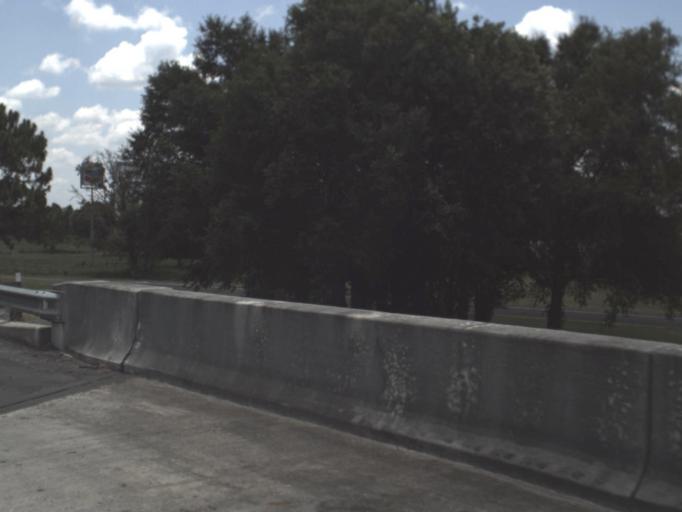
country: US
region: Florida
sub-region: Madison County
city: Madison
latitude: 30.3796
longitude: -83.2974
